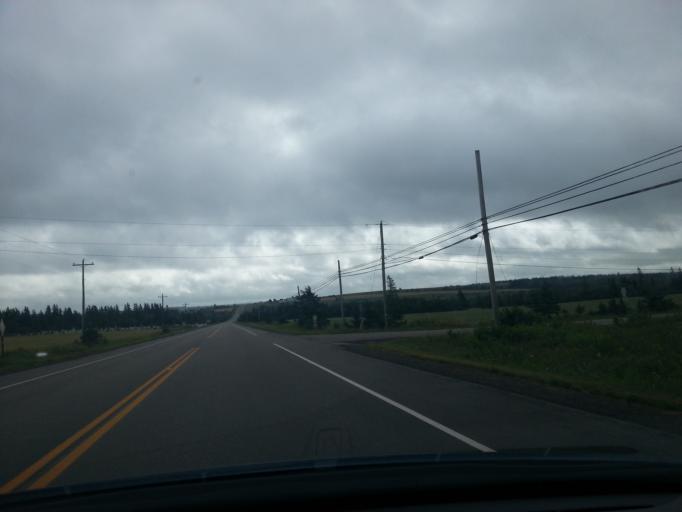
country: CA
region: Prince Edward Island
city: Montague
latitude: 46.4133
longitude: -62.6378
